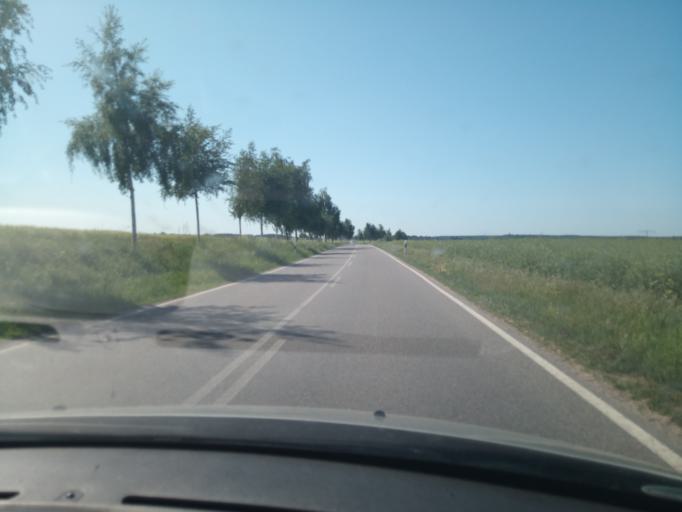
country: DE
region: Mecklenburg-Vorpommern
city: Burg Stargard
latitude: 53.5184
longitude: 13.3174
